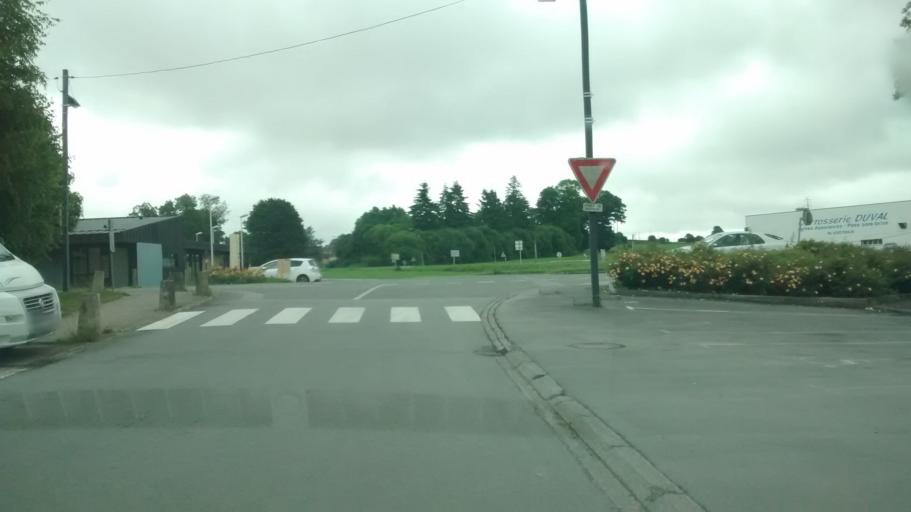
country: FR
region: Brittany
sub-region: Departement du Morbihan
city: Serent
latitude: 47.8210
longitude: -2.5061
